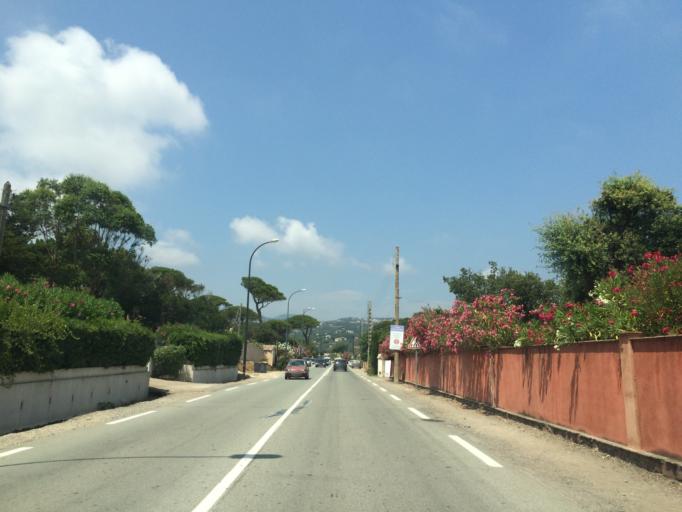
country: FR
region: Provence-Alpes-Cote d'Azur
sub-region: Departement du Var
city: Sainte-Maxime
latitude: 43.3144
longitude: 6.6690
